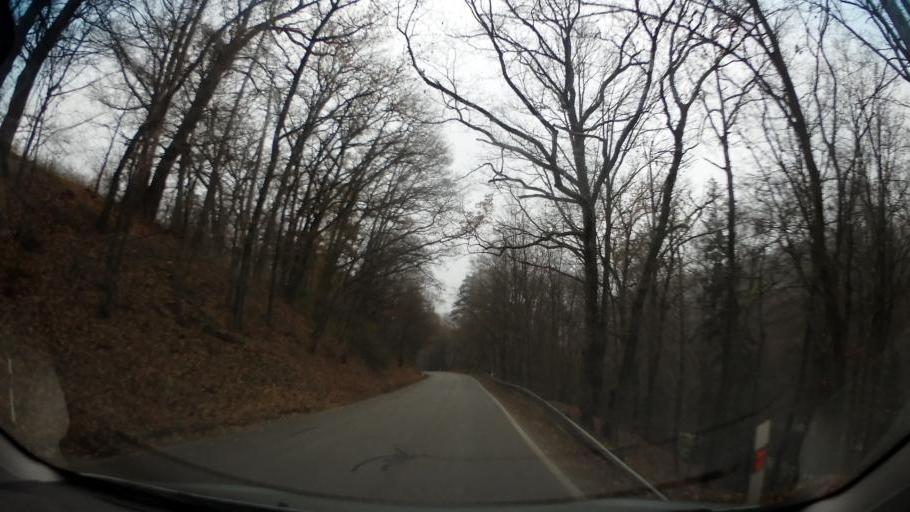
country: CZ
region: Vysocina
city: Mohelno
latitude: 49.1442
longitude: 16.1998
